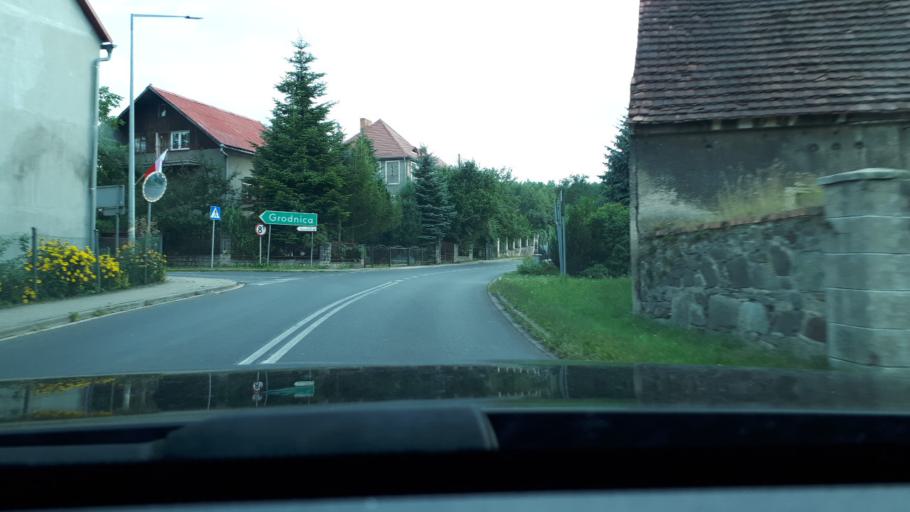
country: PL
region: Lower Silesian Voivodeship
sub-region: Powiat lubanski
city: Lesna
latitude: 51.0663
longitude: 15.2913
